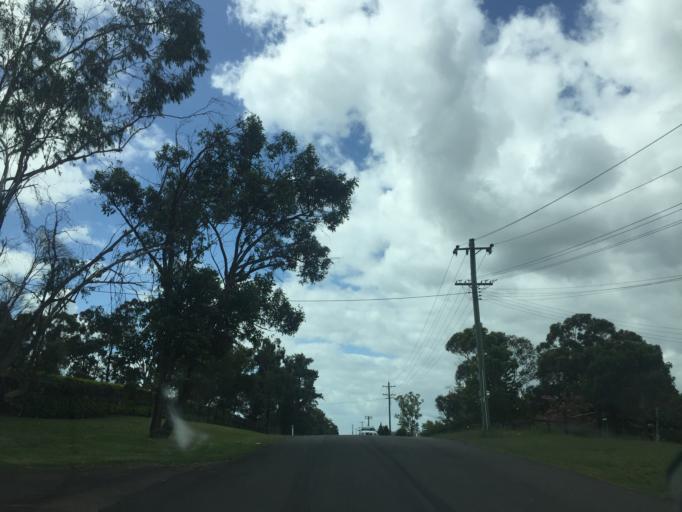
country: AU
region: New South Wales
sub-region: Penrith Municipality
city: Kingswood Park
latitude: -33.7978
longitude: 150.7319
